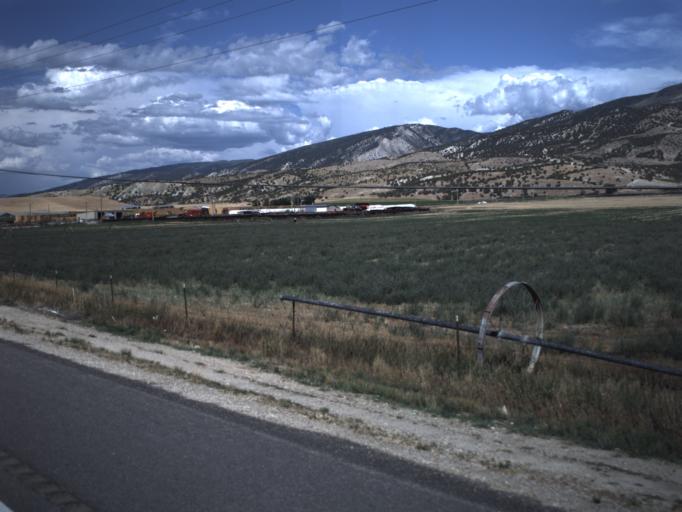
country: US
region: Utah
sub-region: Sanpete County
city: Manti
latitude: 39.2903
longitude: -111.6244
